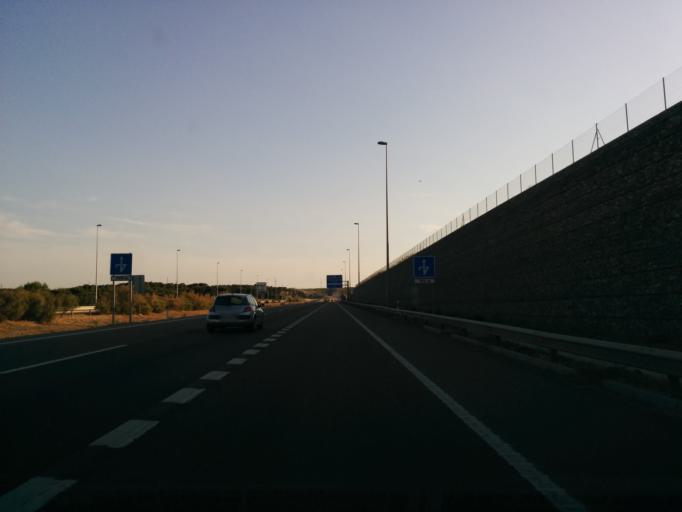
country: ES
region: Aragon
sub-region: Provincia de Zaragoza
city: Zaragoza
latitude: 41.6162
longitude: -0.8692
